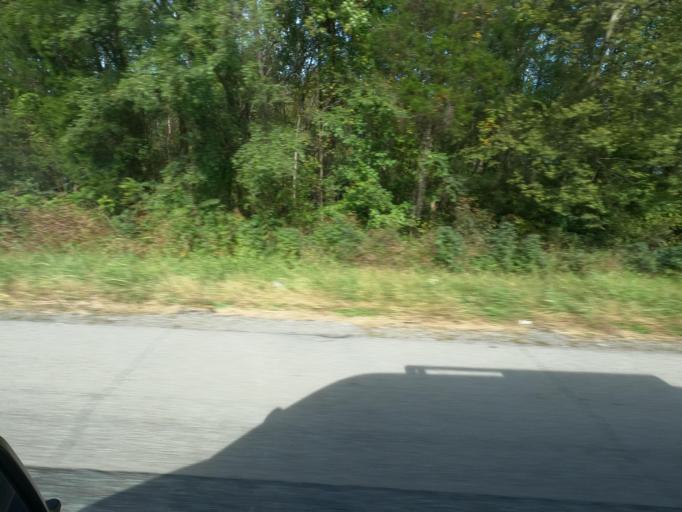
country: US
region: Tennessee
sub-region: Humphreys County
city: New Johnsonville
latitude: 35.8680
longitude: -87.8812
